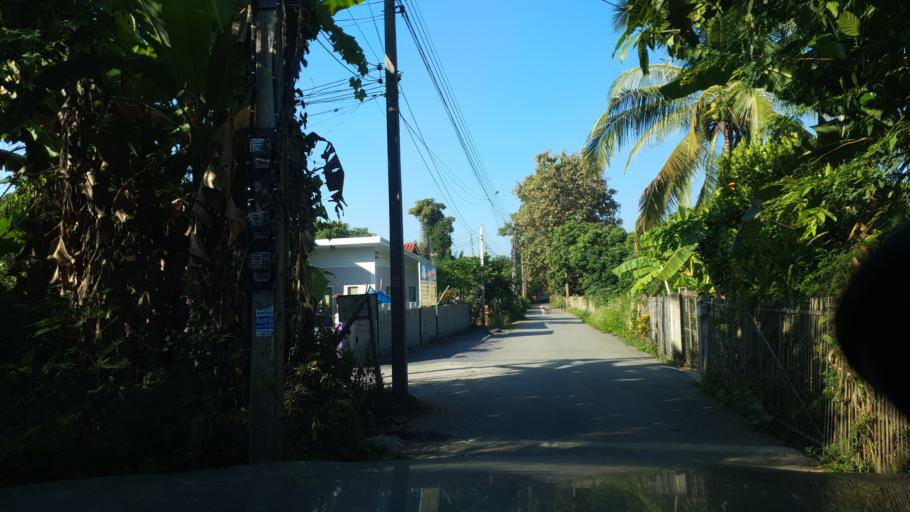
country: TH
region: Chiang Mai
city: Mae On
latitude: 18.7414
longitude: 99.1945
